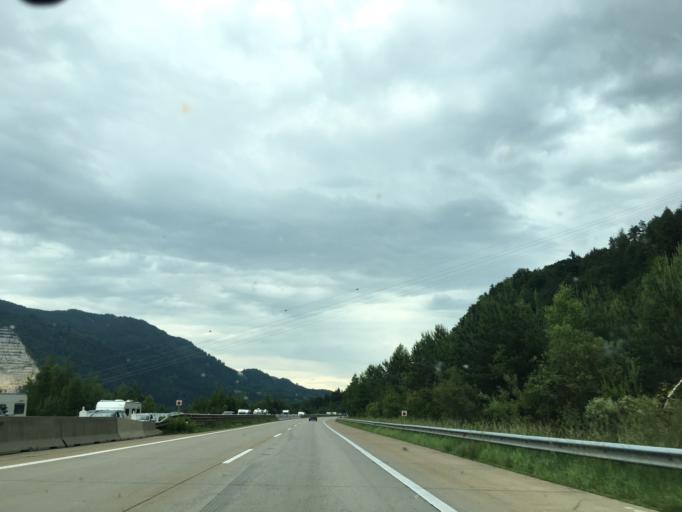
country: AT
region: Carinthia
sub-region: Villach Stadt
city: Villach
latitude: 46.6474
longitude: 13.7690
